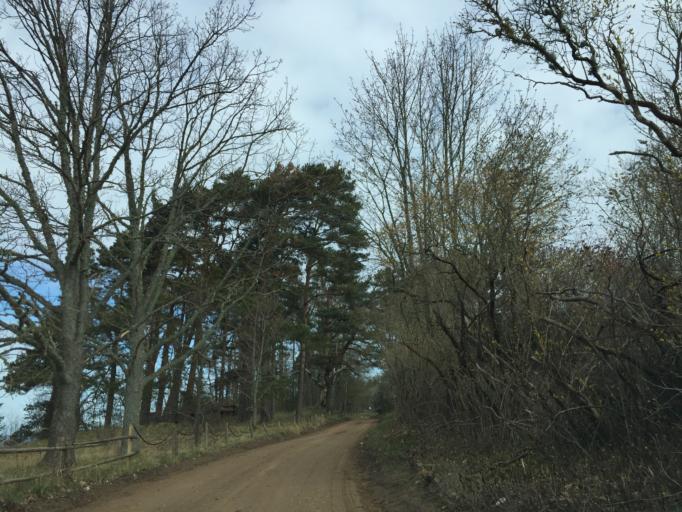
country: LV
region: Salacgrivas
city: Salacgriva
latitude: 57.5171
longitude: 24.3797
